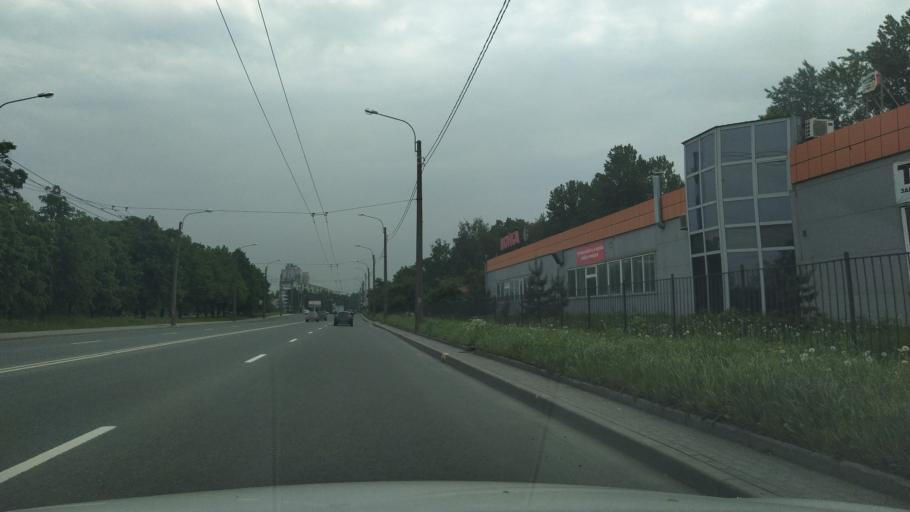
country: RU
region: St.-Petersburg
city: Kupchino
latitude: 59.8762
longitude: 30.3541
